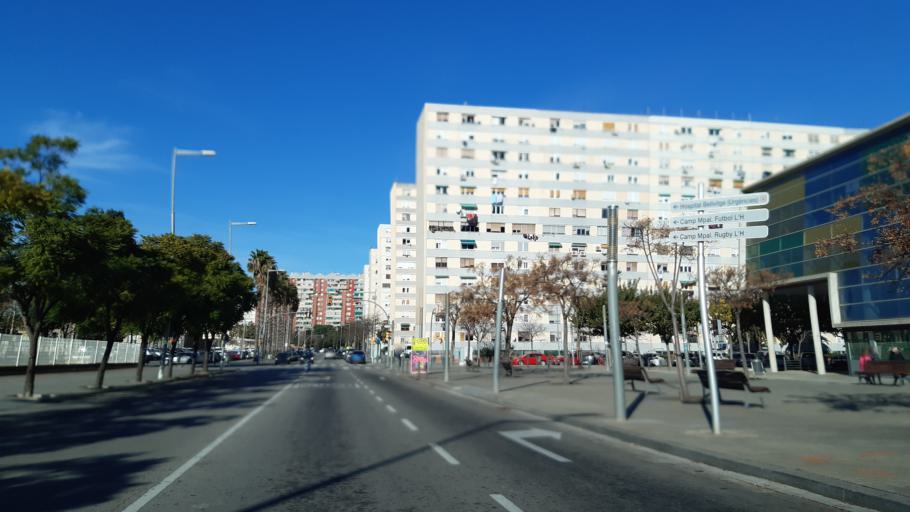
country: ES
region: Catalonia
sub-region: Provincia de Barcelona
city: L'Hospitalet de Llobregat
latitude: 41.3467
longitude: 2.1075
